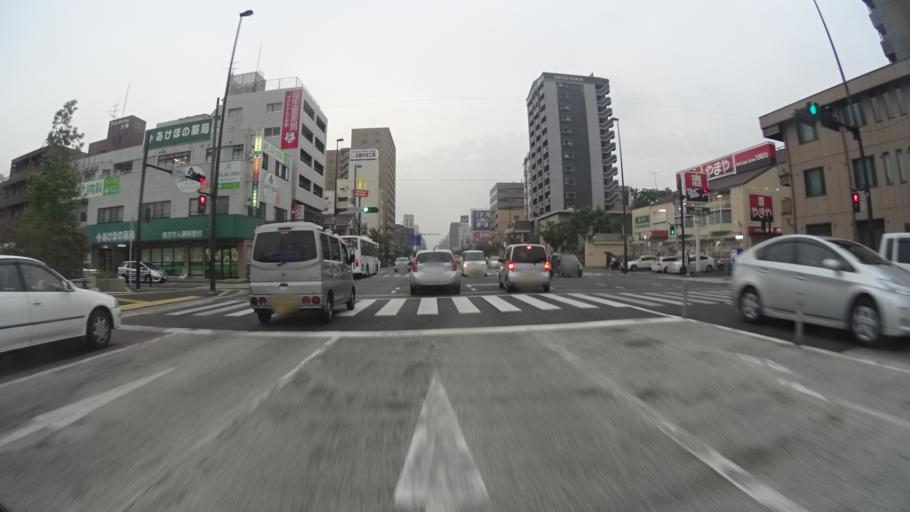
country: JP
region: Fukuoka
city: Fukuoka-shi
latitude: 33.5733
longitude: 130.4141
